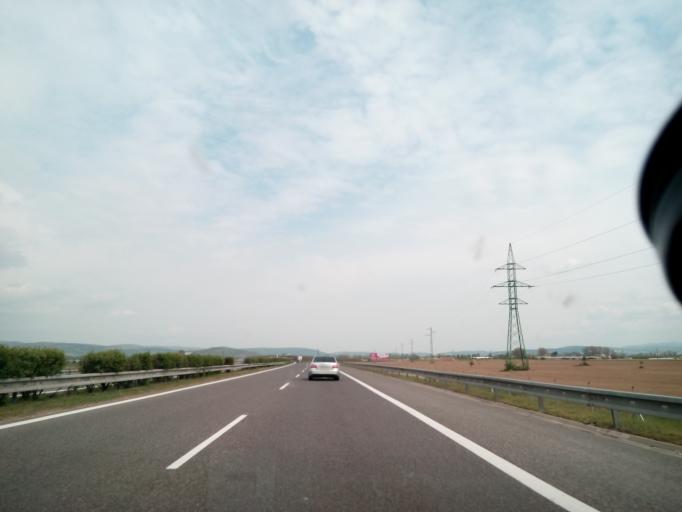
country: SK
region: Trenciansky
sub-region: Okres Trencin
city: Trencin
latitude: 48.8406
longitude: 17.9397
